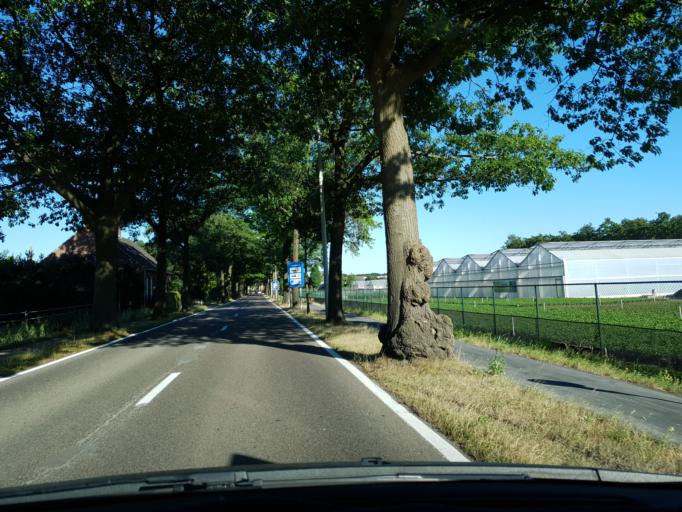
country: NL
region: North Brabant
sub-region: Gemeente Zundert
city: Zundert
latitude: 51.4596
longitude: 4.6992
